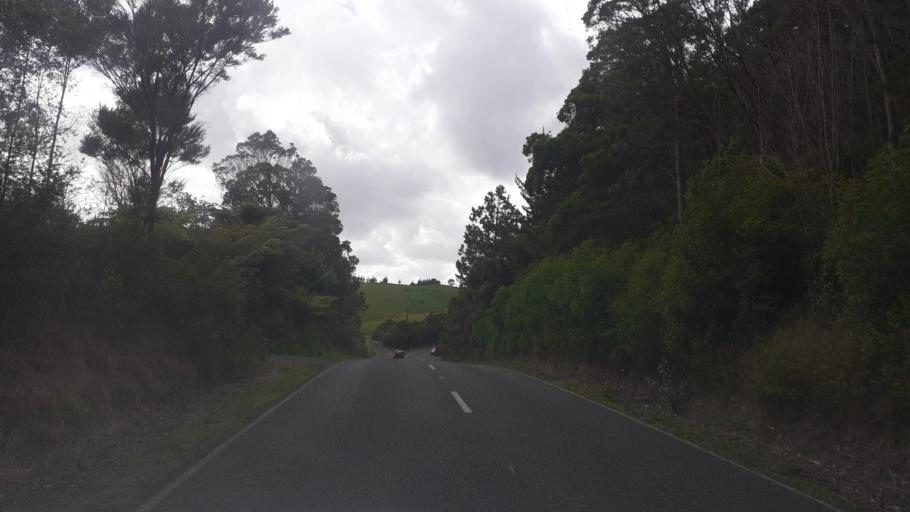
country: NZ
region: Northland
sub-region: Far North District
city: Kerikeri
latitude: -35.2183
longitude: 173.9934
